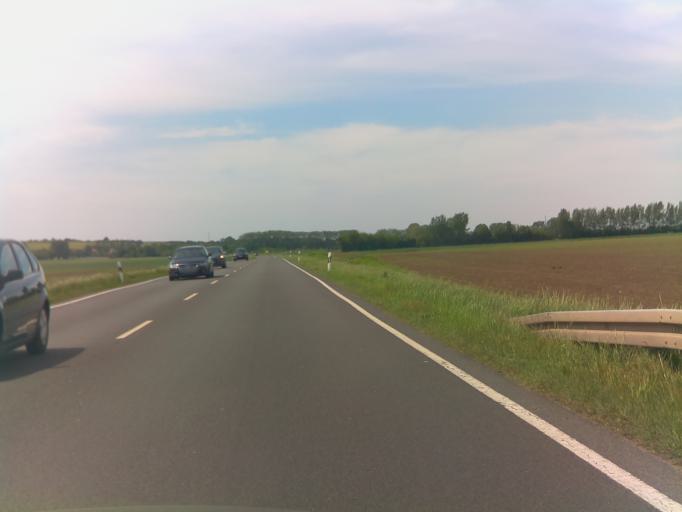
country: DE
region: Saxony-Anhalt
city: Kroppenstedt
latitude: 51.9404
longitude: 11.3488
